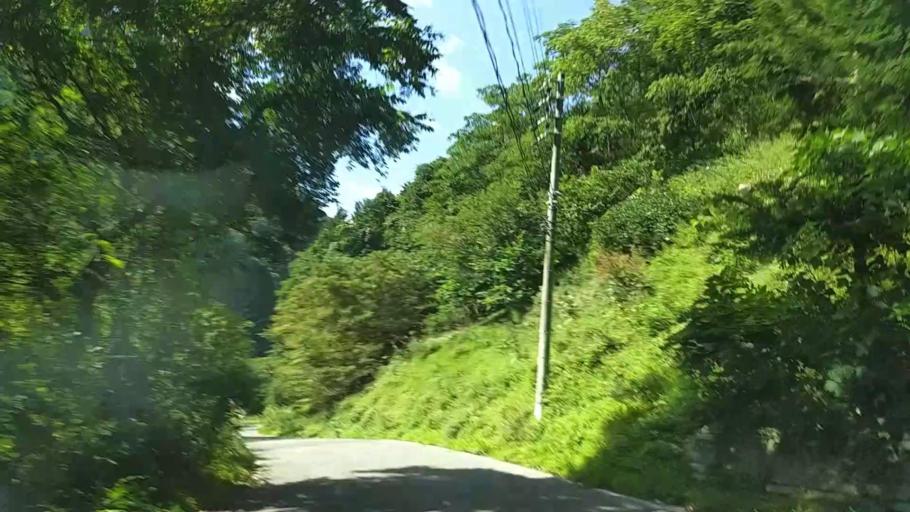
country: JP
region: Nagano
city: Matsumoto
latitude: 36.2026
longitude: 138.0864
